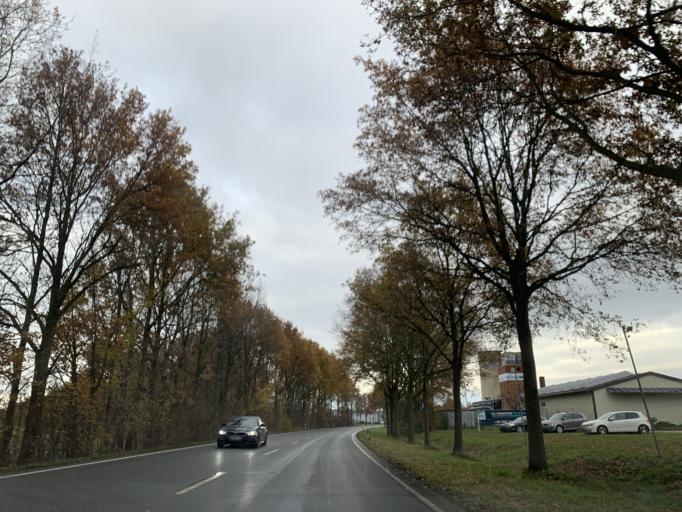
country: NL
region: Overijssel
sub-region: Gemeente Enschede
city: Enschede
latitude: 52.1331
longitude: 6.9090
